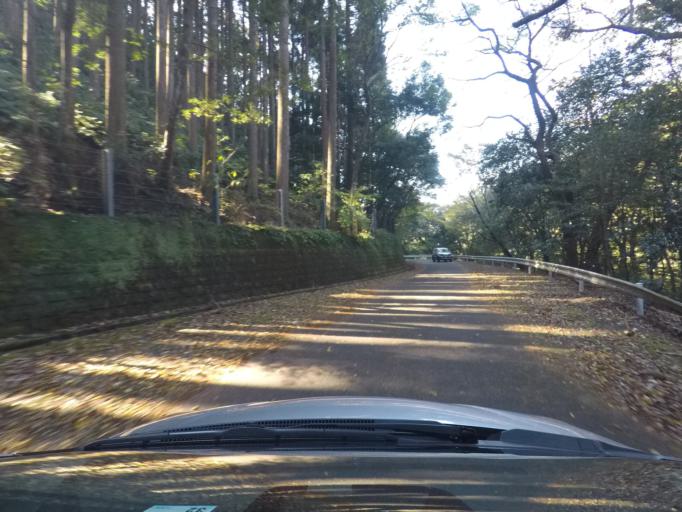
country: JP
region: Miyazaki
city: Kobayashi
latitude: 32.0235
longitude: 131.1905
